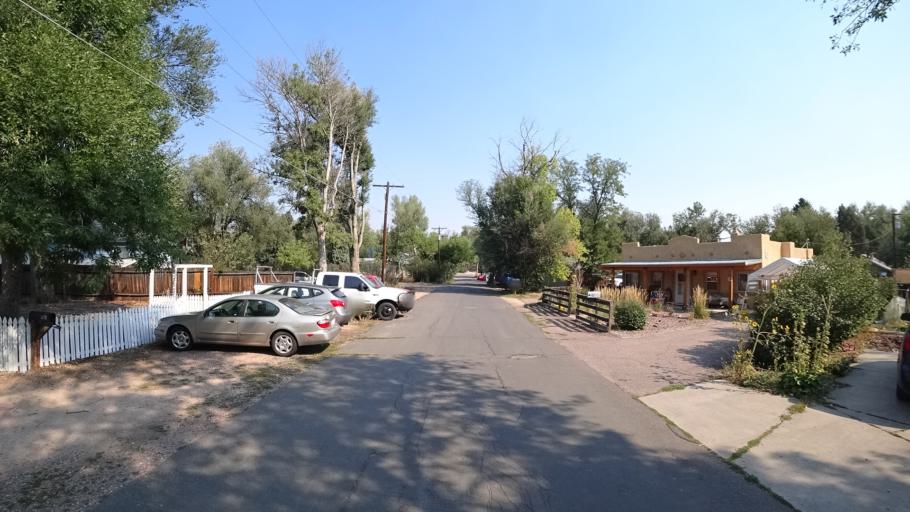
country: US
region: Colorado
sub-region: El Paso County
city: Colorado Springs
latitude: 38.8083
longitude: -104.8314
